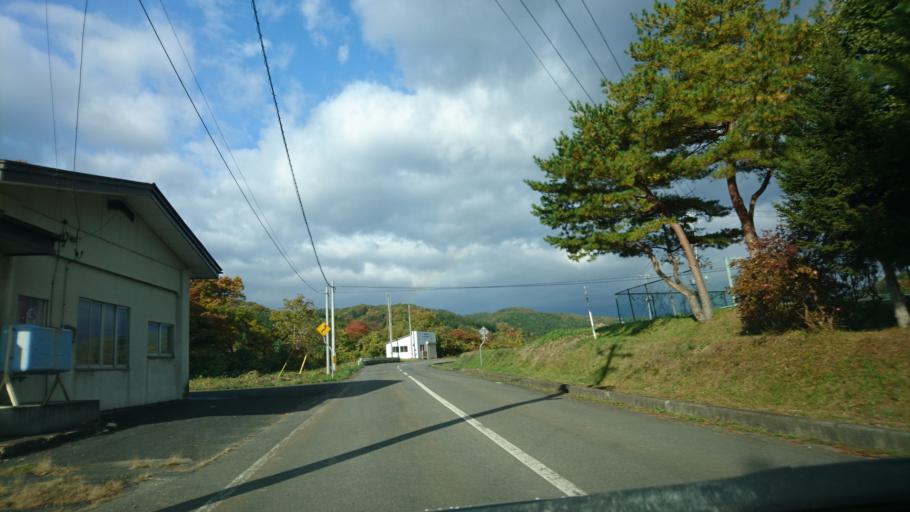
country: JP
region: Iwate
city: Mizusawa
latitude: 39.0863
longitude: 140.9865
